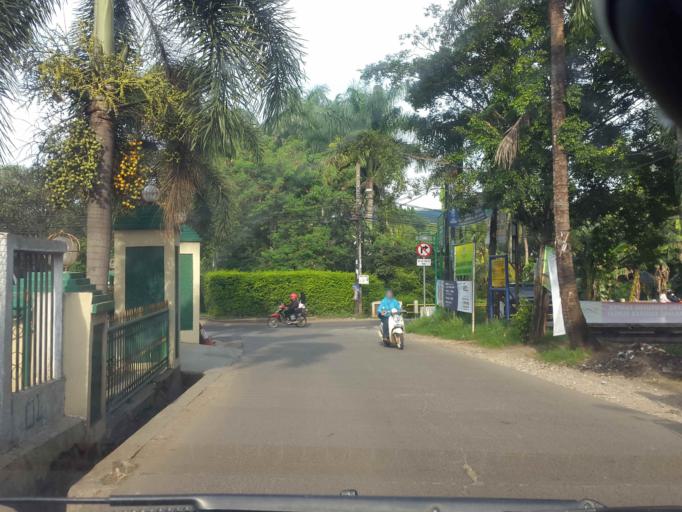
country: ID
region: Banten
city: South Tangerang
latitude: -6.2809
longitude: 106.6973
